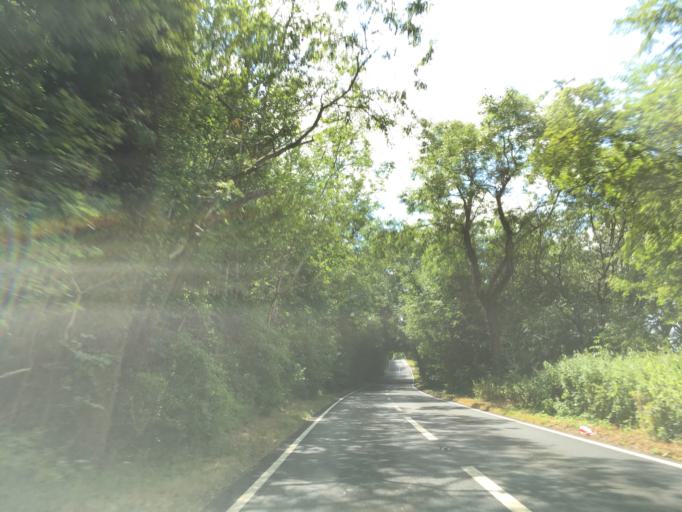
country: GB
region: England
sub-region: Gloucestershire
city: Painswick
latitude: 51.8041
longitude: -2.1955
